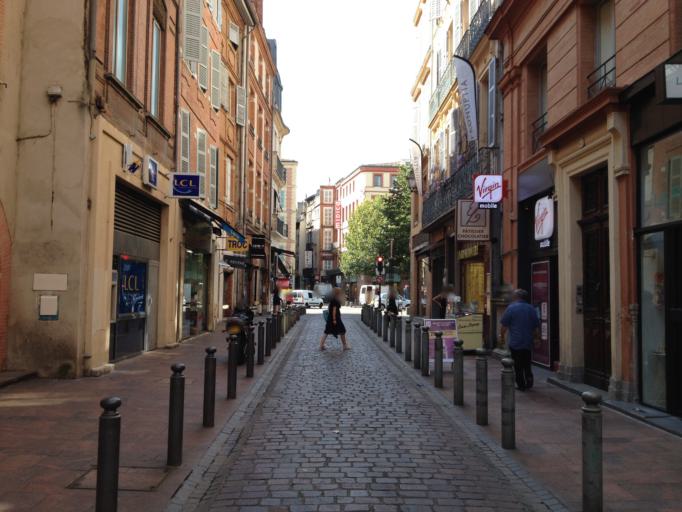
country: FR
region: Midi-Pyrenees
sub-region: Departement de la Haute-Garonne
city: Toulouse
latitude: 43.6010
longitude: 1.4451
